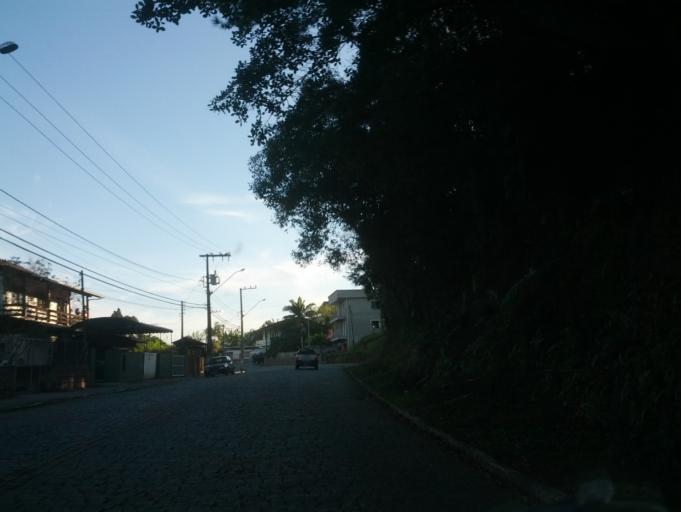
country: BR
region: Santa Catarina
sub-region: Indaial
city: Indaial
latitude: -26.8972
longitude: -49.2442
